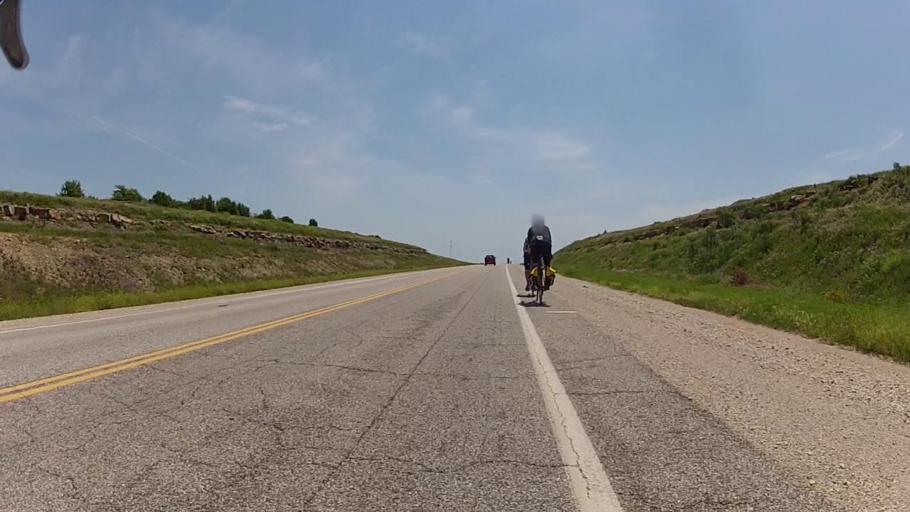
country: US
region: Kansas
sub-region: Chautauqua County
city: Sedan
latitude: 37.1140
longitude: -96.4708
